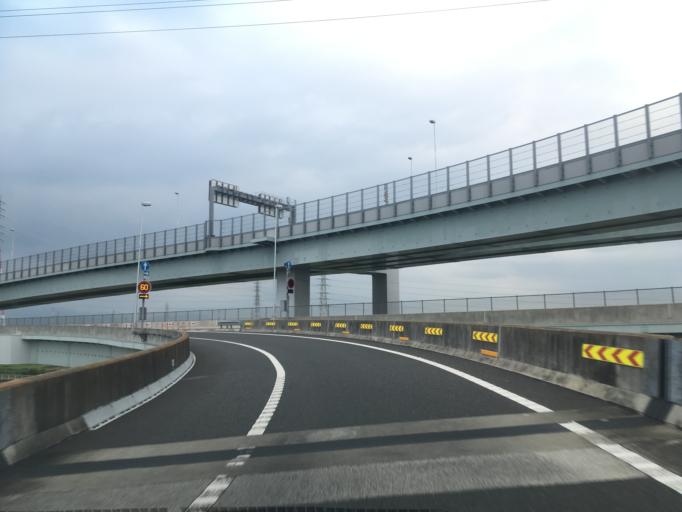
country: JP
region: Kanagawa
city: Chigasaki
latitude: 35.3503
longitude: 139.3922
